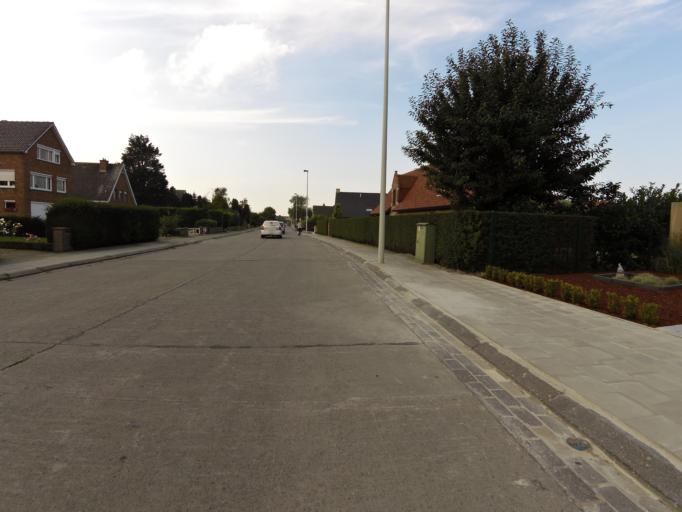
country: BE
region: Flanders
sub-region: Provincie West-Vlaanderen
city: Ostend
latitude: 51.2036
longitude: 2.9124
